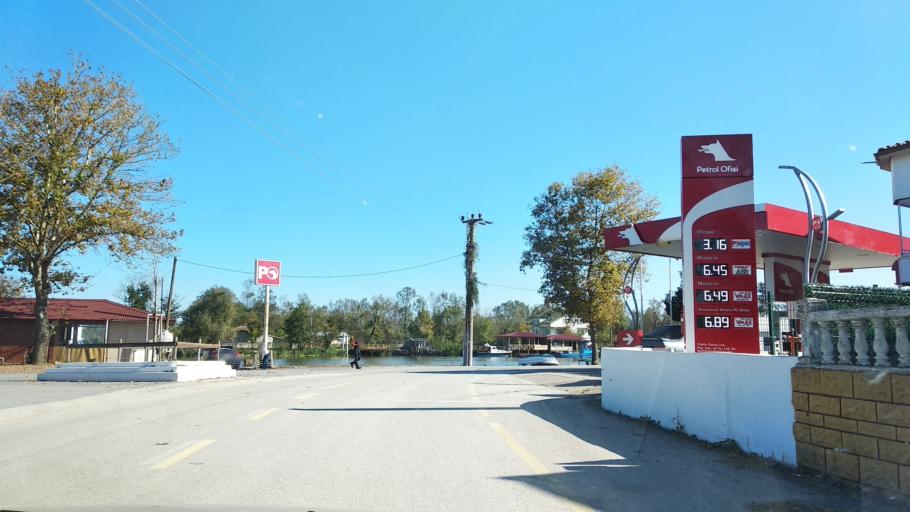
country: TR
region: Sakarya
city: Karasu
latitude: 41.1184
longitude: 30.6447
